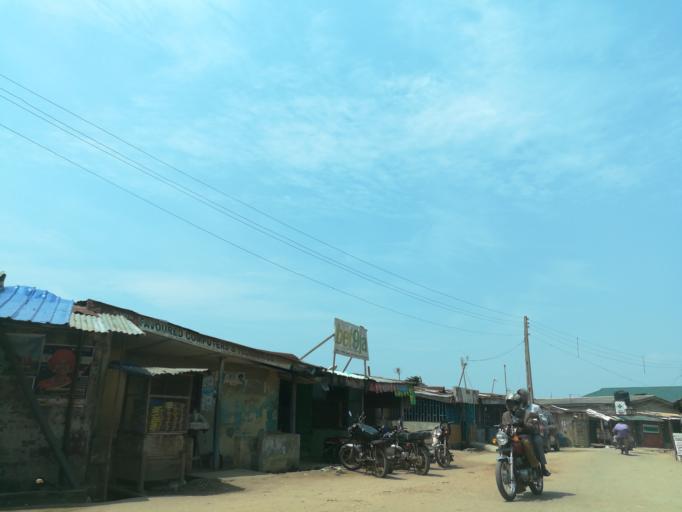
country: NG
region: Lagos
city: Ikorodu
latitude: 6.6202
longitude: 3.4978
